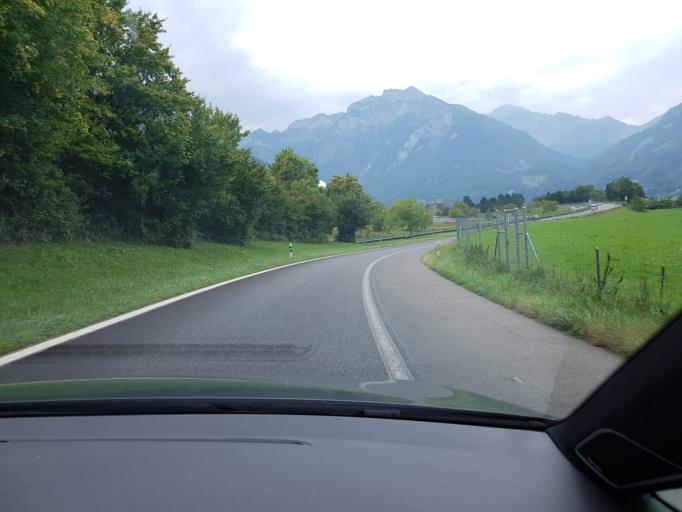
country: CH
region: Bern
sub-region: Interlaken-Oberhasli District
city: Matten
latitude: 46.6856
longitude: 7.8785
